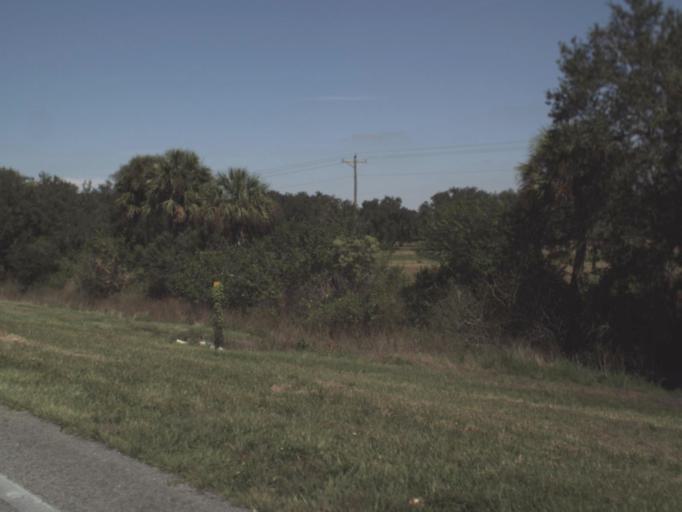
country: US
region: Florida
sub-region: Hendry County
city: Port LaBelle
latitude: 26.9603
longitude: -81.3164
